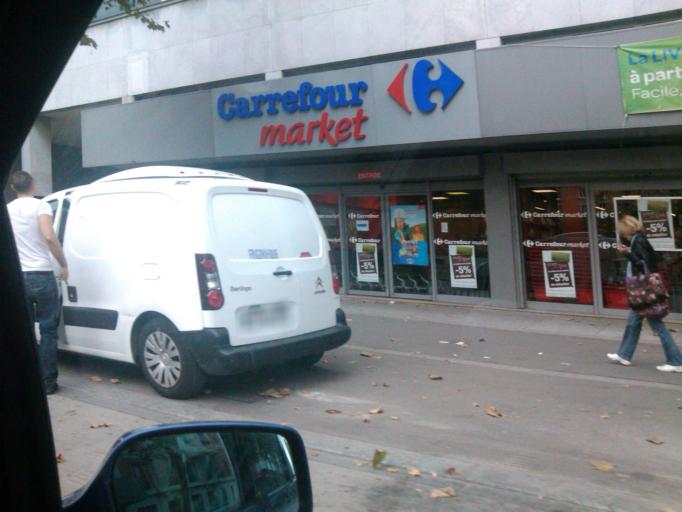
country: FR
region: Ile-de-France
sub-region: Departement des Hauts-de-Seine
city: Montrouge
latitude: 48.8260
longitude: 2.3193
